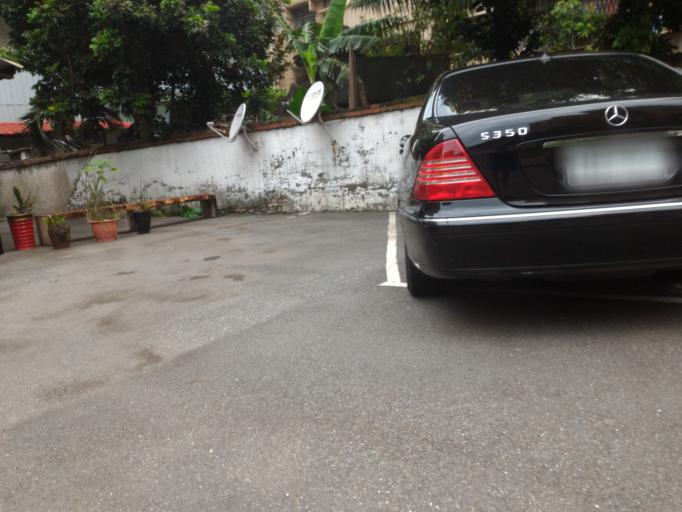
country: TW
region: Taipei
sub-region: Taipei
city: Banqiao
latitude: 24.9906
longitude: 121.4219
